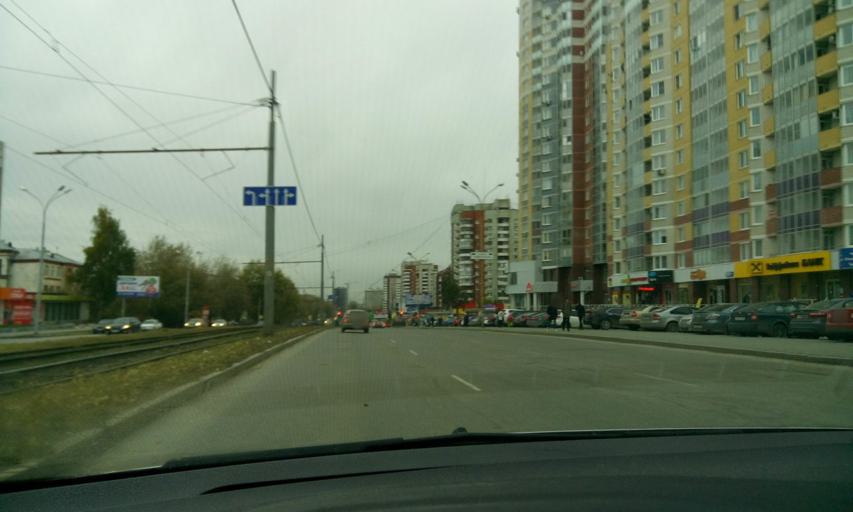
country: RU
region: Sverdlovsk
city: Yekaterinburg
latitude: 56.8530
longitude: 60.6385
